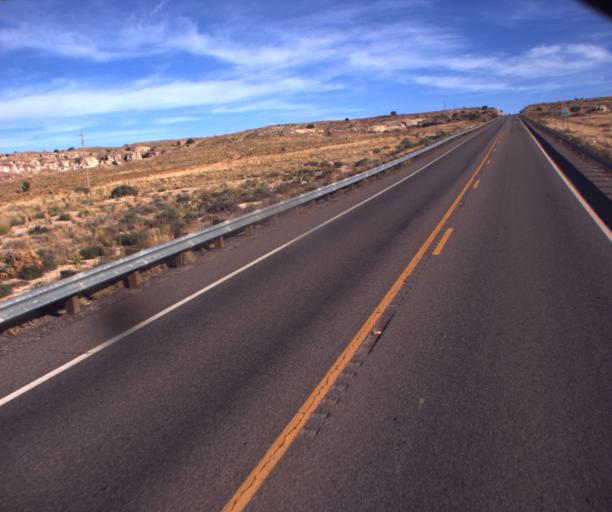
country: US
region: New Mexico
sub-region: San Juan County
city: Shiprock
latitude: 36.9285
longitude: -109.1010
